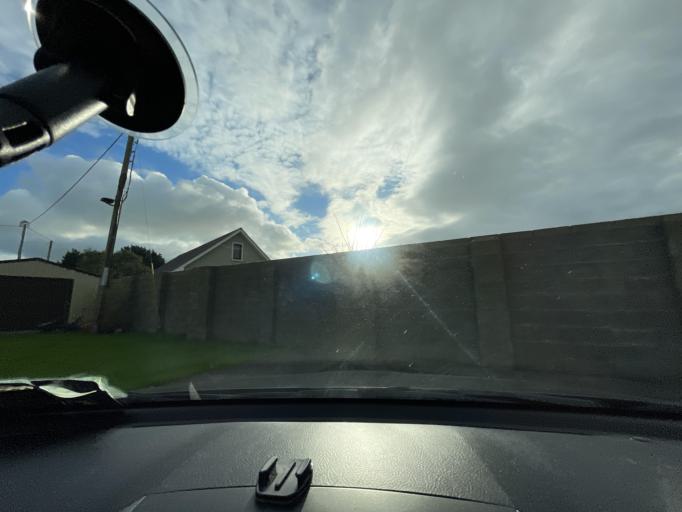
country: IE
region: Leinster
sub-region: Lu
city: Clogherhead
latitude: 53.7935
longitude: -6.2402
